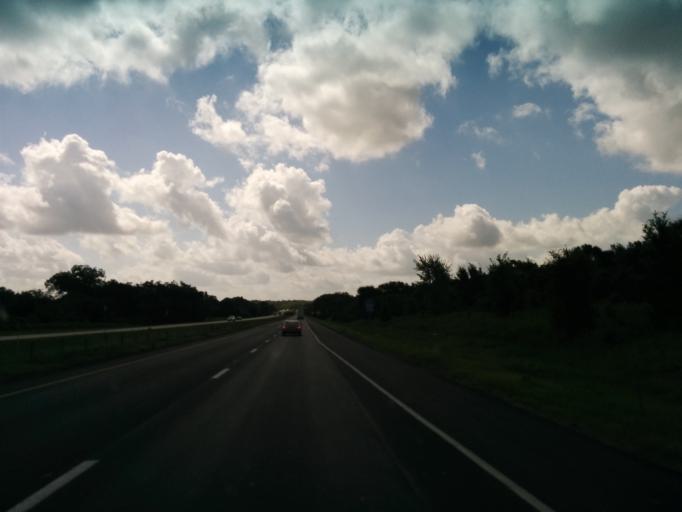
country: US
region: Texas
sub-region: Fayette County
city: Schulenburg
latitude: 29.6923
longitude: -96.8444
